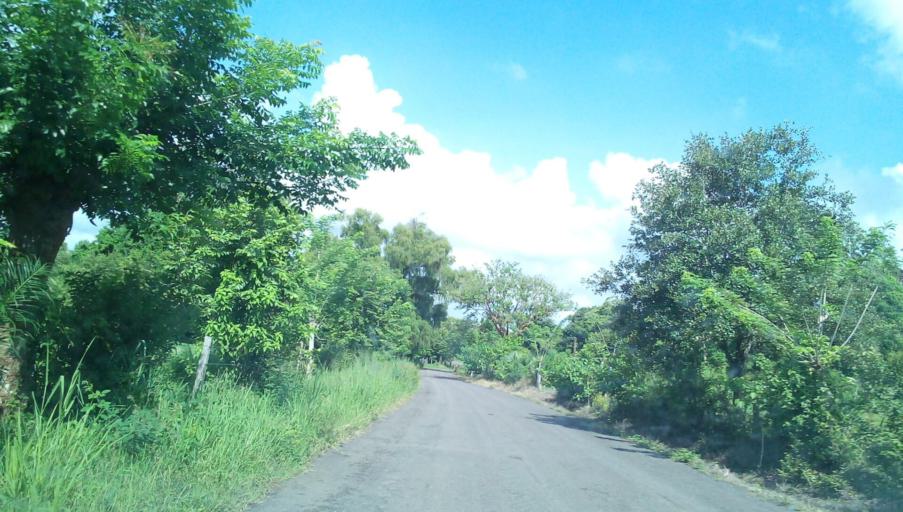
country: MX
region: Veracruz
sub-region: Citlaltepetl
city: Las Sabinas
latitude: 21.3422
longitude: -97.8867
